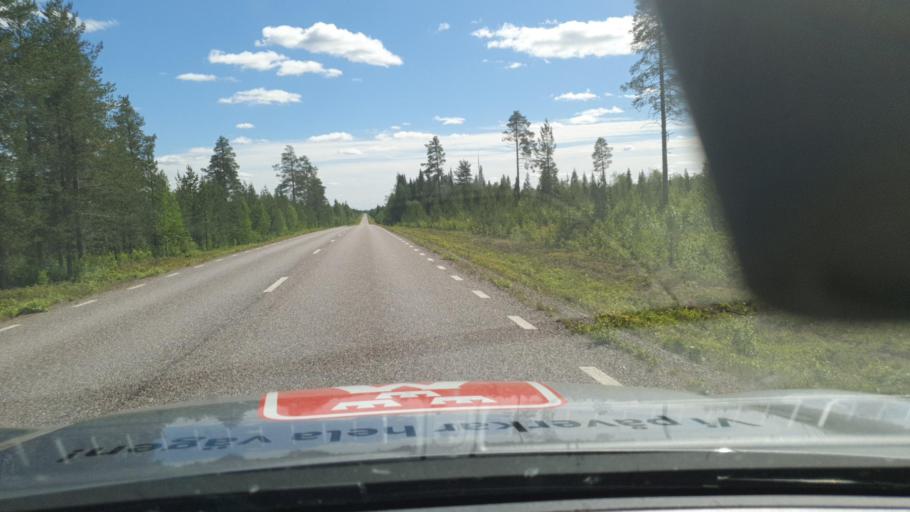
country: SE
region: Norrbotten
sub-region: Pajala Kommun
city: Pajala
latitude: 67.1498
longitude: 23.5609
